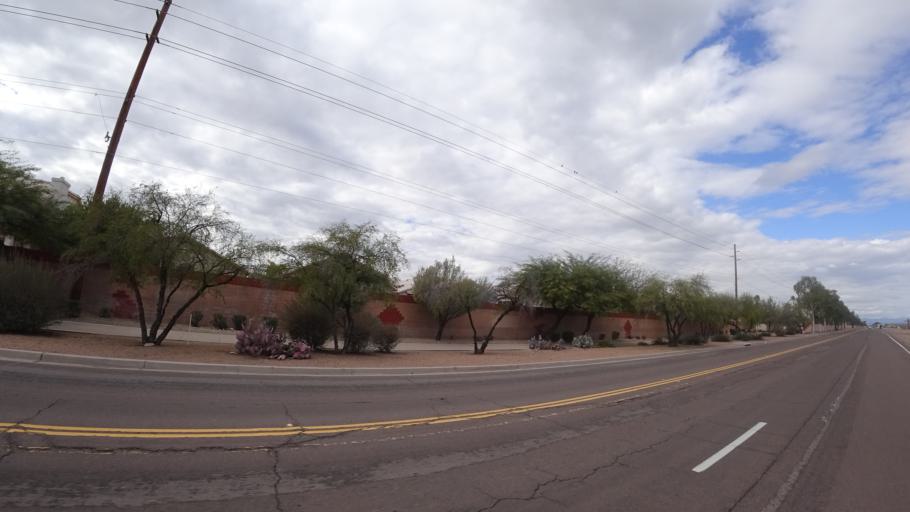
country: US
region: Arizona
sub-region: Maricopa County
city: Scottsdale
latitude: 33.4827
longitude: -111.8917
